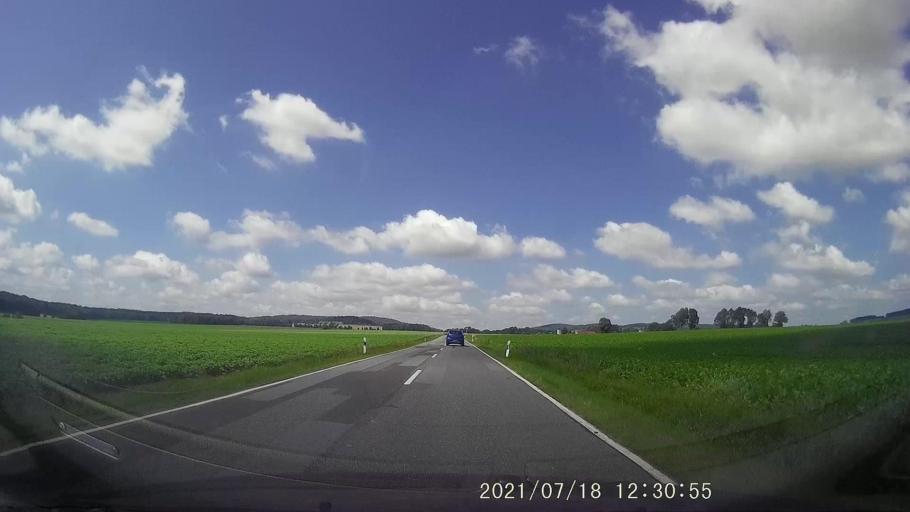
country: DE
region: Saxony
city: Konigshain
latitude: 51.1747
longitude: 14.9035
